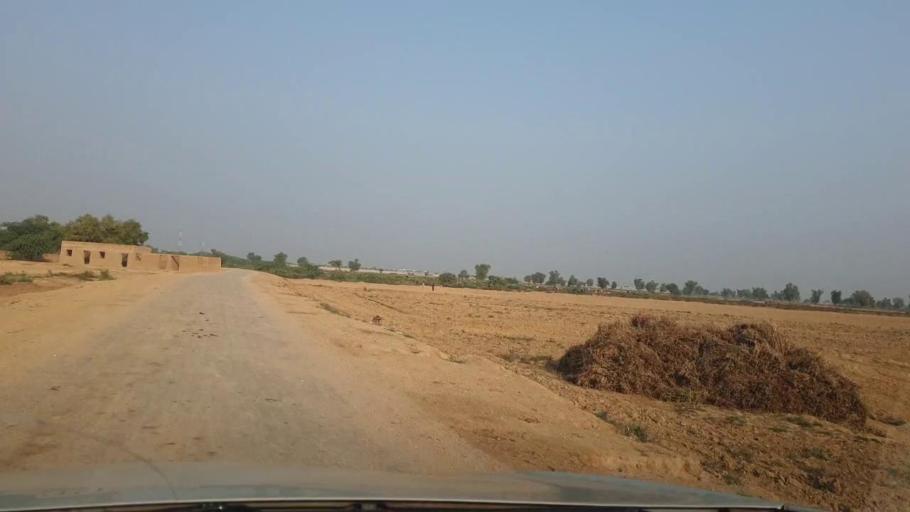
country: PK
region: Sindh
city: Sehwan
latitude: 26.3351
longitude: 67.7313
